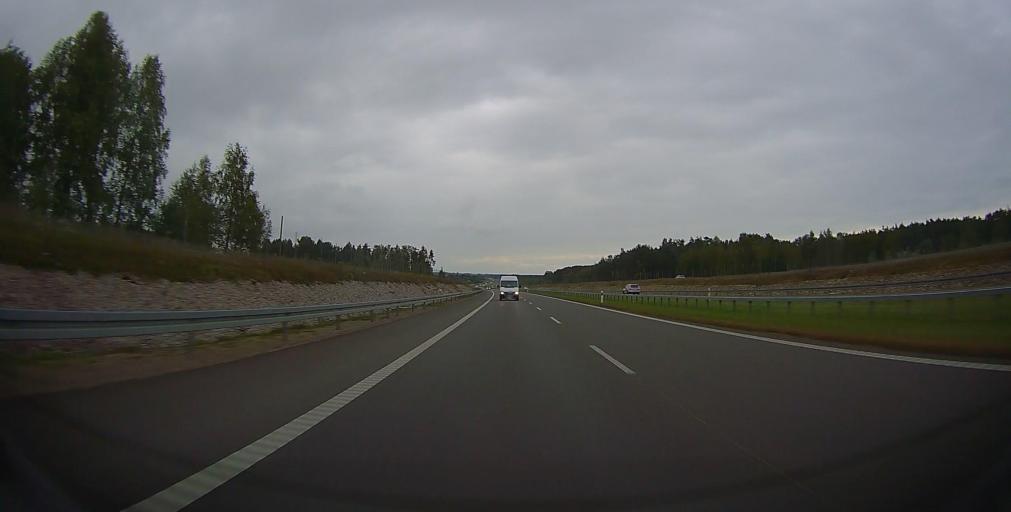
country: PL
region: Masovian Voivodeship
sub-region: Powiat radomski
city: Zakrzew
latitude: 51.4764
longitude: 21.0586
